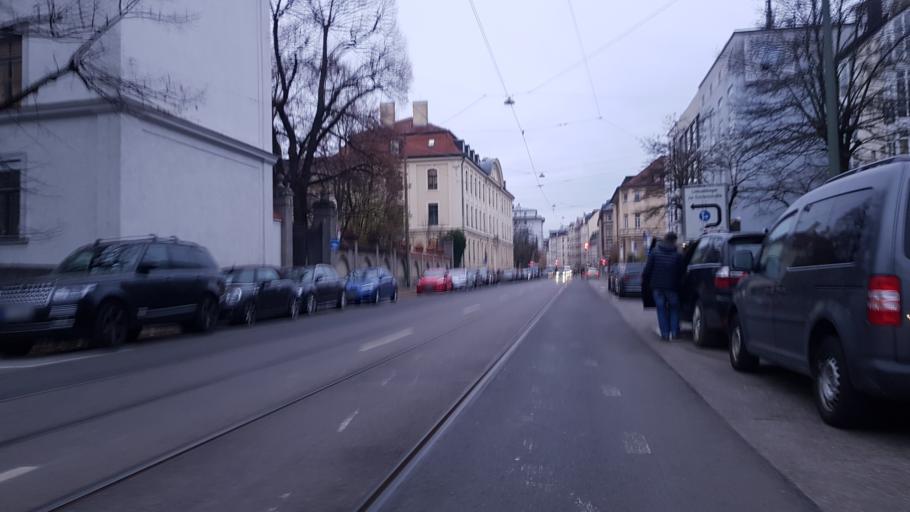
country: DE
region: Bavaria
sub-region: Upper Bavaria
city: Bogenhausen
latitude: 48.1384
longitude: 11.5990
